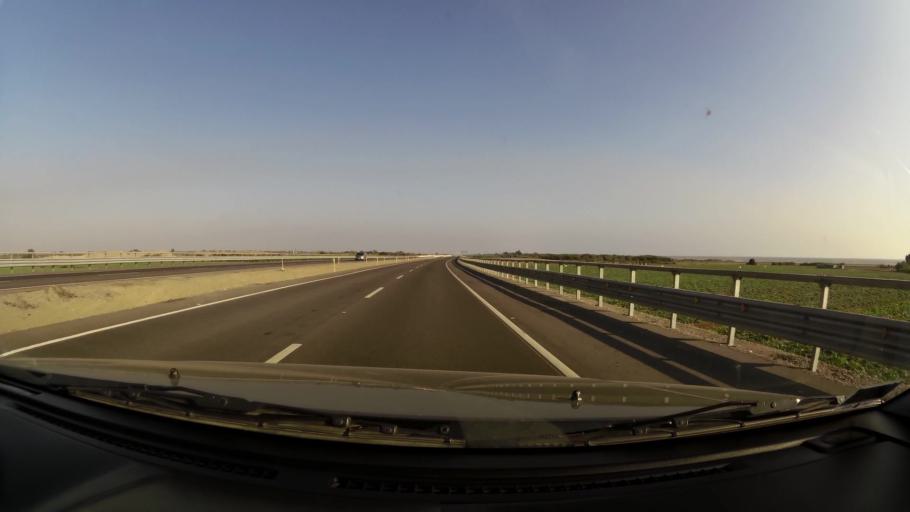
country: PE
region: Ica
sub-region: Provincia de Chincha
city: Chincha Baja
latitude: -13.5222
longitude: -76.1831
